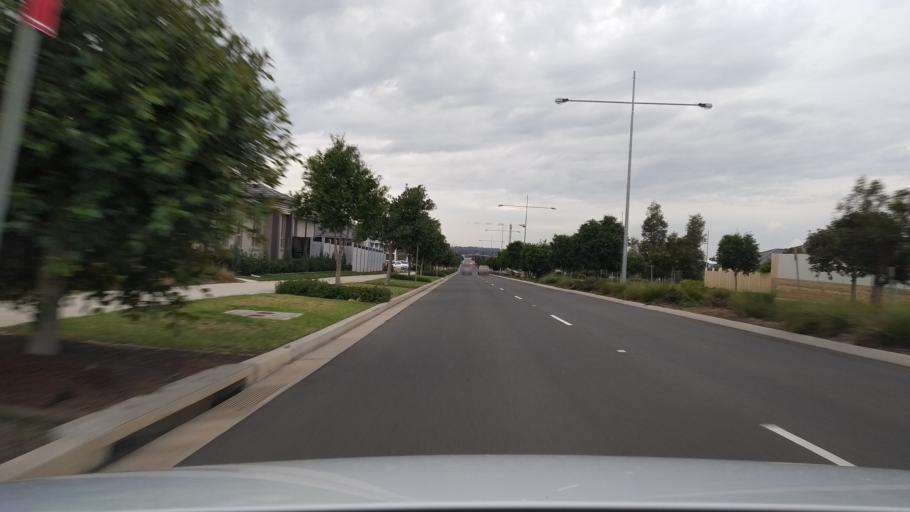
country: AU
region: New South Wales
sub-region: Camden
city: Narellan
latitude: -34.0041
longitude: 150.7306
